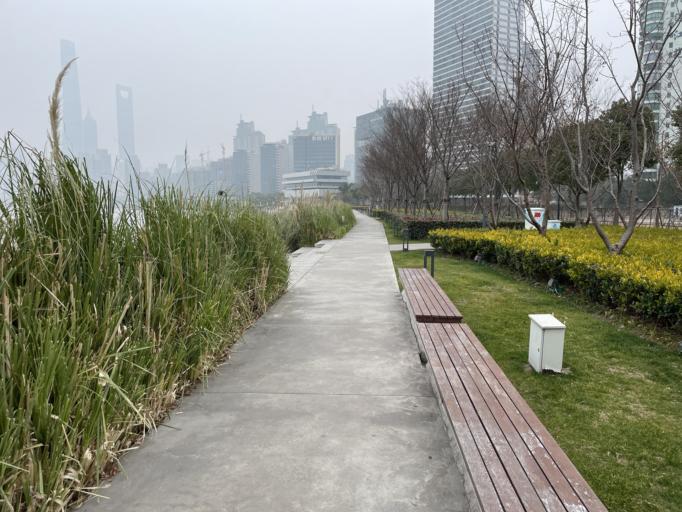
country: CN
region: Shanghai Shi
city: Pudong
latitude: 31.2153
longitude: 121.5074
